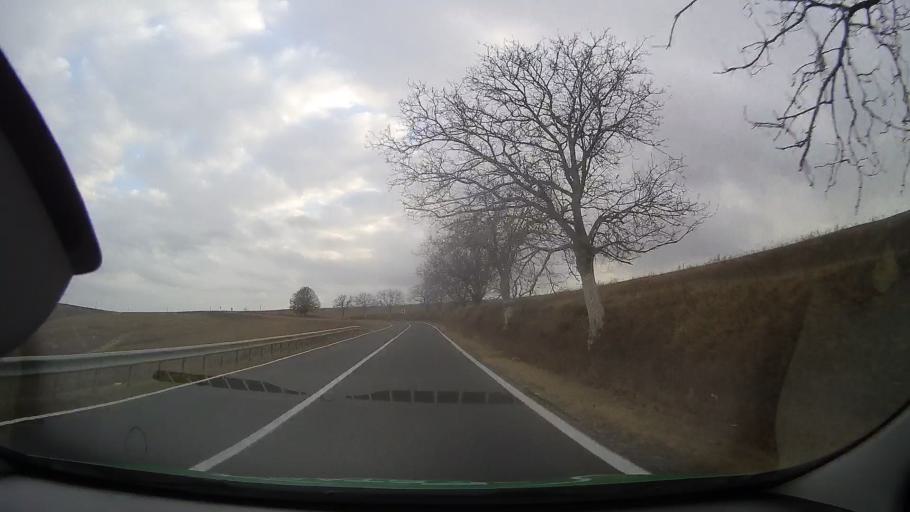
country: RO
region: Constanta
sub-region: Comuna Deleni
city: Deleni
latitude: 44.0964
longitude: 28.0168
